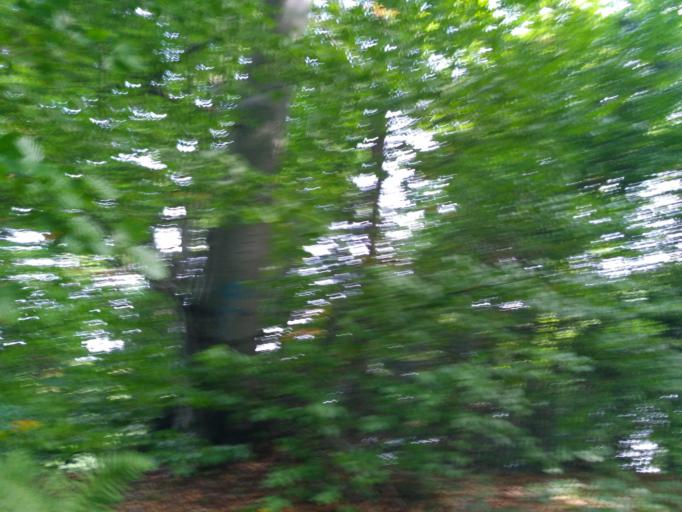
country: PL
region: Subcarpathian Voivodeship
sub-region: Powiat strzyzowski
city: Frysztak
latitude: 49.8895
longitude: 21.5361
